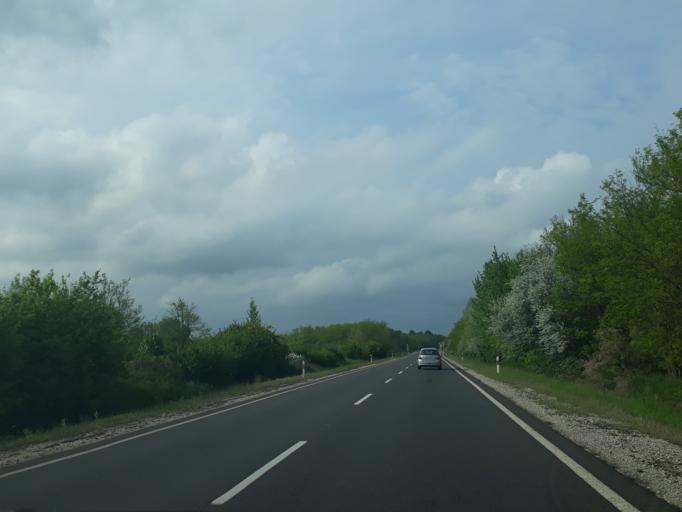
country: HU
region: Szabolcs-Szatmar-Bereg
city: Nyirtass
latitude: 48.0940
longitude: 21.9872
